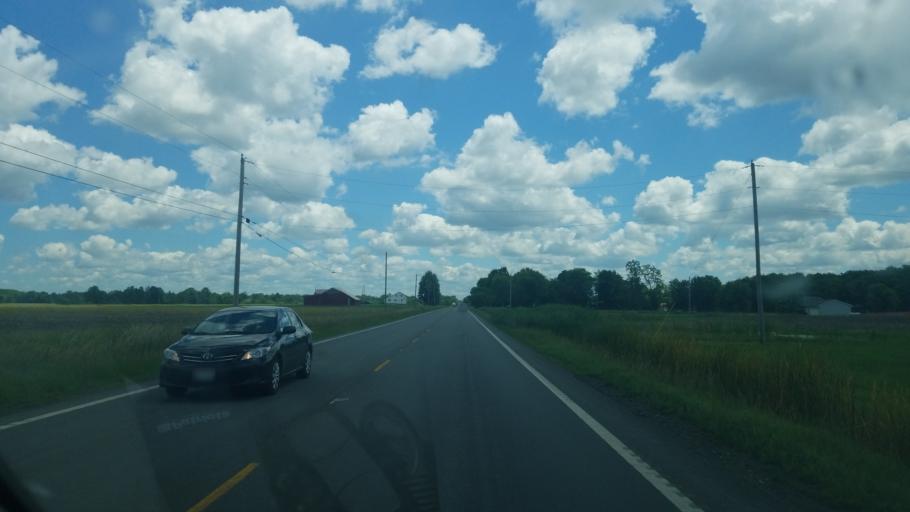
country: US
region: Ohio
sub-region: Huron County
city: New London
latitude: 41.0296
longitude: -82.3809
